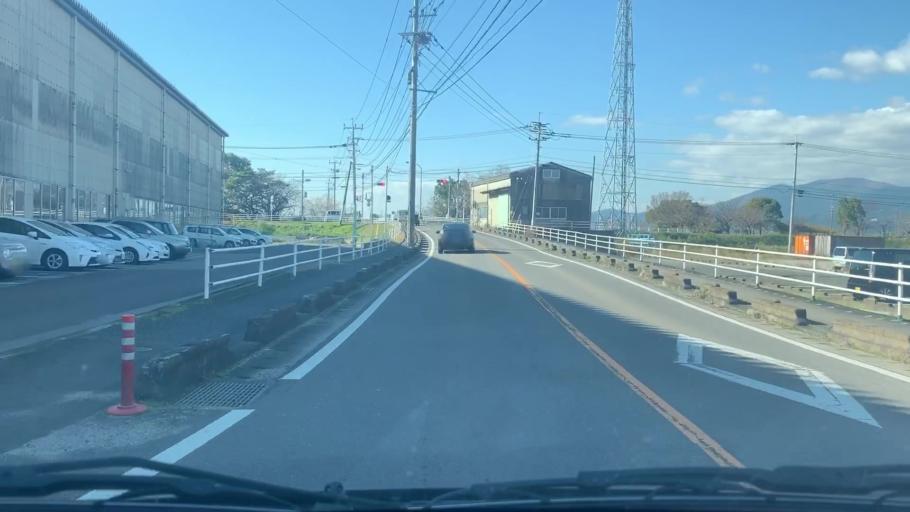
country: JP
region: Saga Prefecture
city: Saga-shi
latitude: 33.2912
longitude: 130.2821
